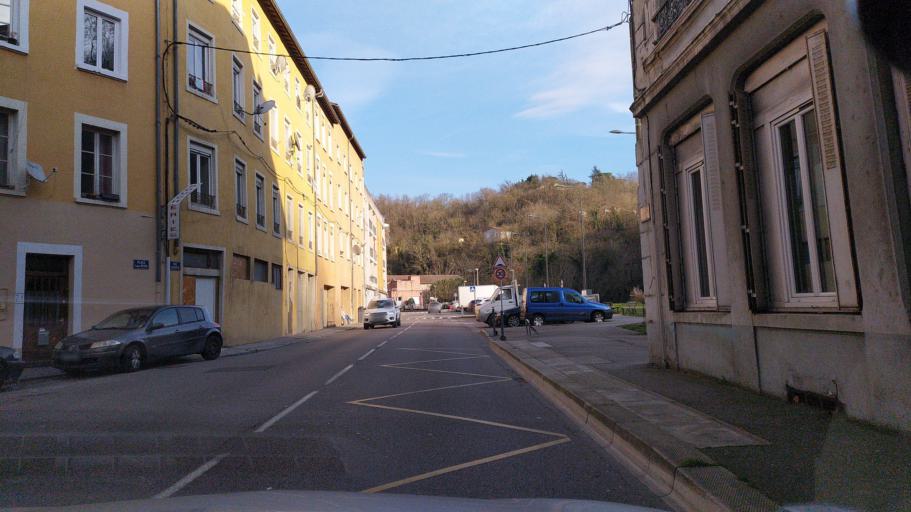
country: FR
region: Rhone-Alpes
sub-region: Departement de l'Isere
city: Vienne
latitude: 45.5249
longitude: 4.8881
